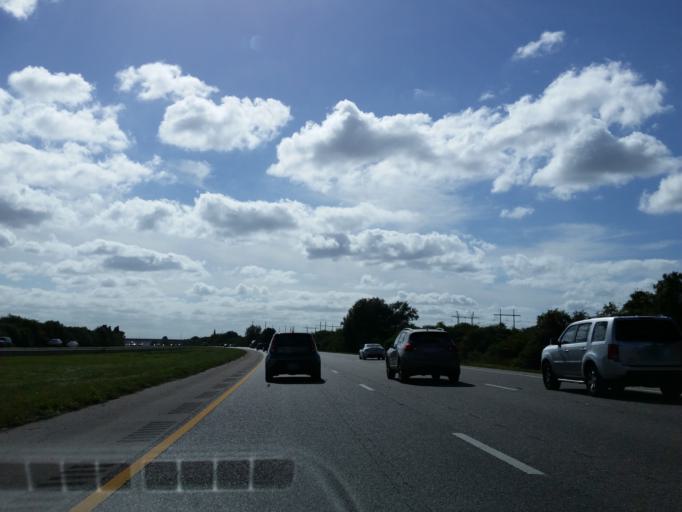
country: US
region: Florida
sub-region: Hillsborough County
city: Sun City Center
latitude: 27.7425
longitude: -82.3825
